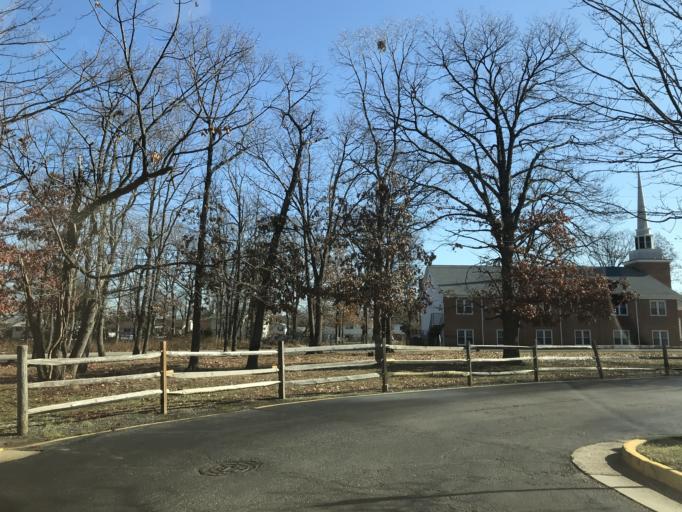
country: US
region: Virginia
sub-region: Fairfax County
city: Franconia
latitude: 38.7793
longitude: -77.1657
